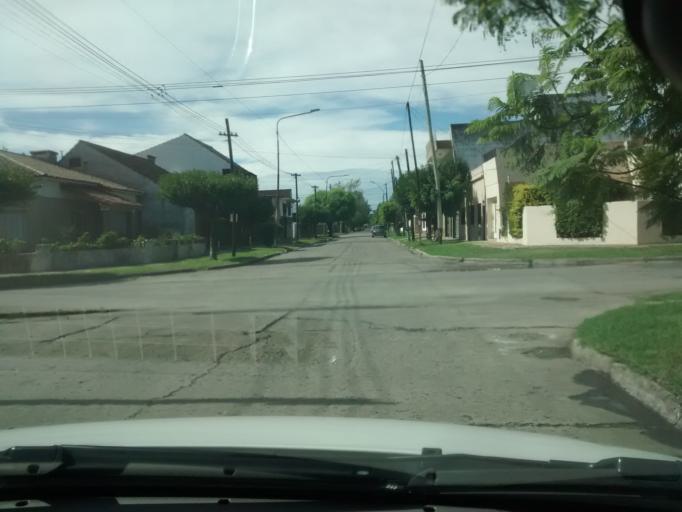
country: AR
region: Buenos Aires
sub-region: Partido de Moron
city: Moron
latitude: -34.6673
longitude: -58.6105
